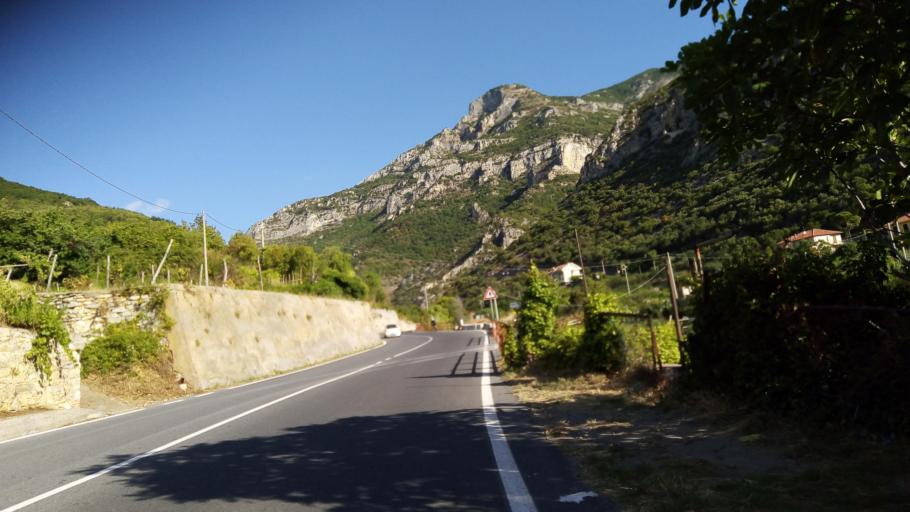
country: IT
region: Liguria
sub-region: Provincia di Savona
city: Toirano
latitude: 44.1296
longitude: 8.2037
